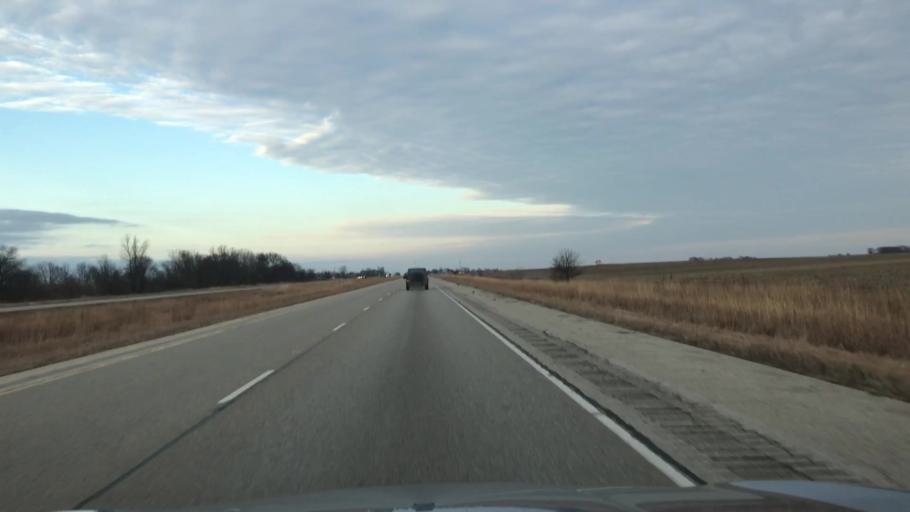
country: US
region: Illinois
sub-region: McLean County
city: Twin Grove
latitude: 40.3856
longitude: -89.0854
